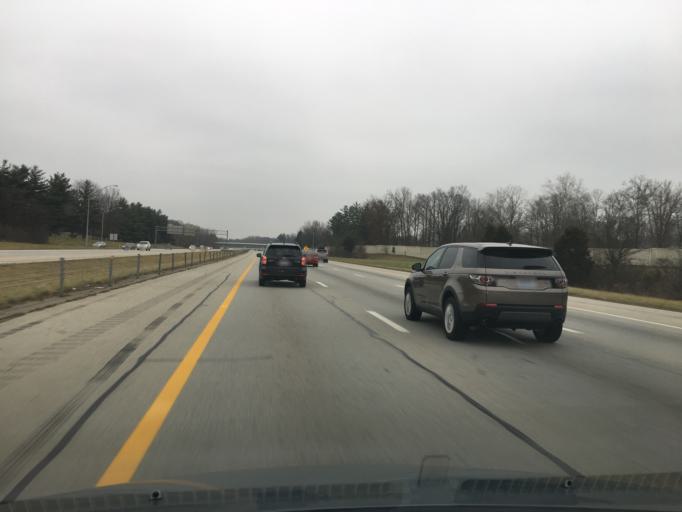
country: US
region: Ohio
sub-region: Hamilton County
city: Sixteen Mile Stand
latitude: 39.2605
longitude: -84.3370
